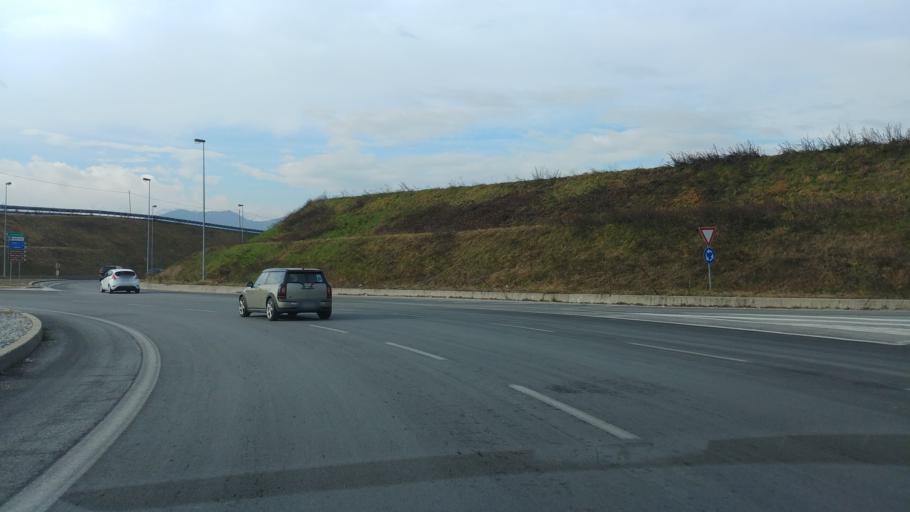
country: IT
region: Piedmont
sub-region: Provincia di Cuneo
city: Cuneo
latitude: 44.3884
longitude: 7.5201
